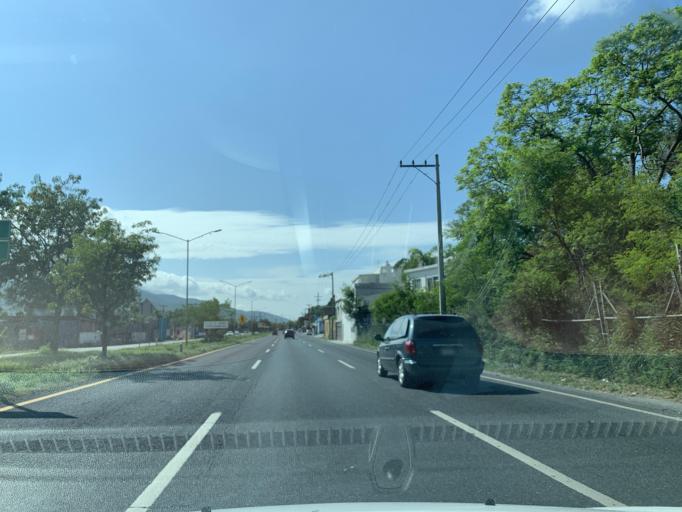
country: MX
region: Nuevo Leon
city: Santiago
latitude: 25.4214
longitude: -100.1456
